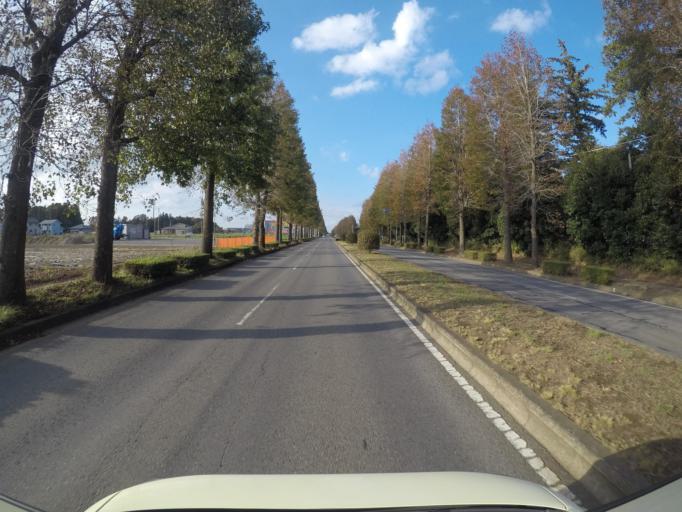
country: JP
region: Ibaraki
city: Naka
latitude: 36.0645
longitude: 140.1012
